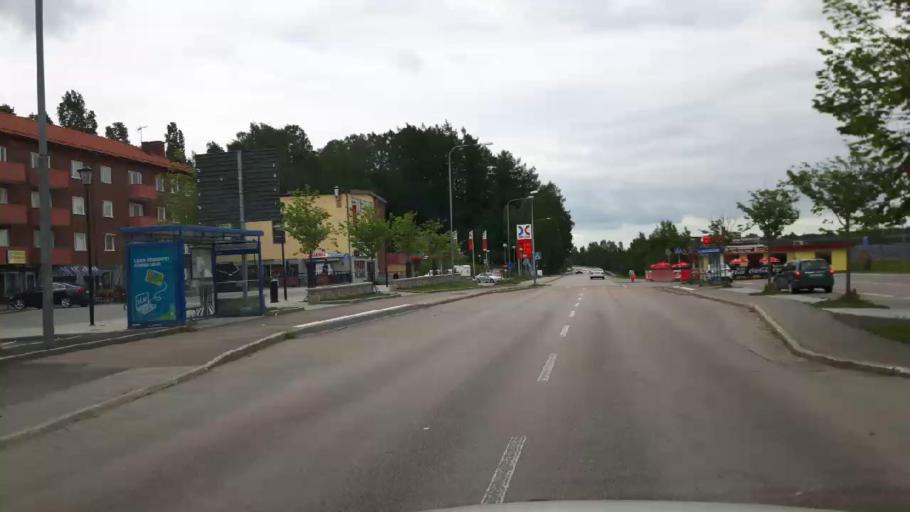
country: SE
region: Vaestmanland
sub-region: Kopings Kommun
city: Kolsva
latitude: 59.6003
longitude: 15.8422
